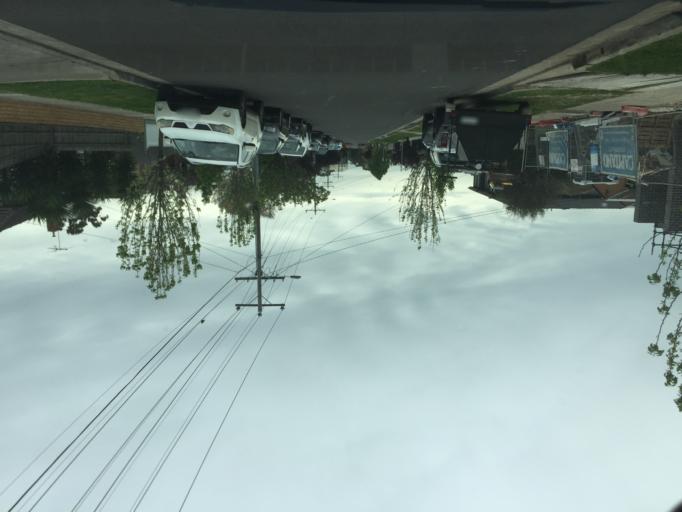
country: AU
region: Victoria
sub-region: Brimbank
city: Sunshine North
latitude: -37.7811
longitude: 144.8343
